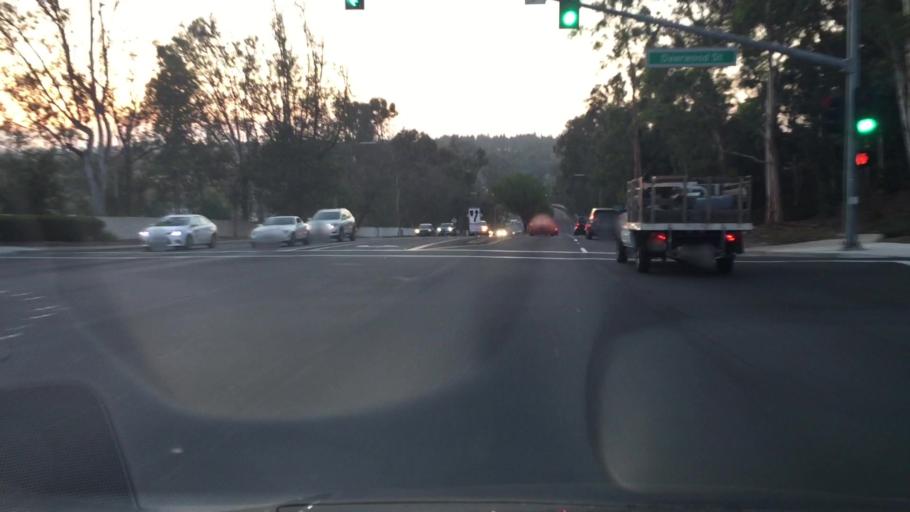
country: US
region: California
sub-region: San Diego County
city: Poway
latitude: 32.9802
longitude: -117.0585
